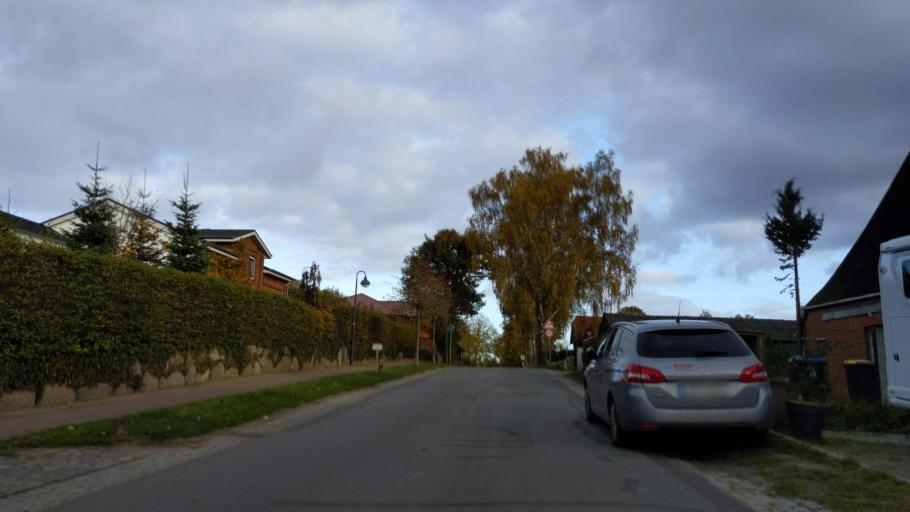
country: DE
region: Schleswig-Holstein
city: Susel
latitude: 54.1050
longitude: 10.7126
